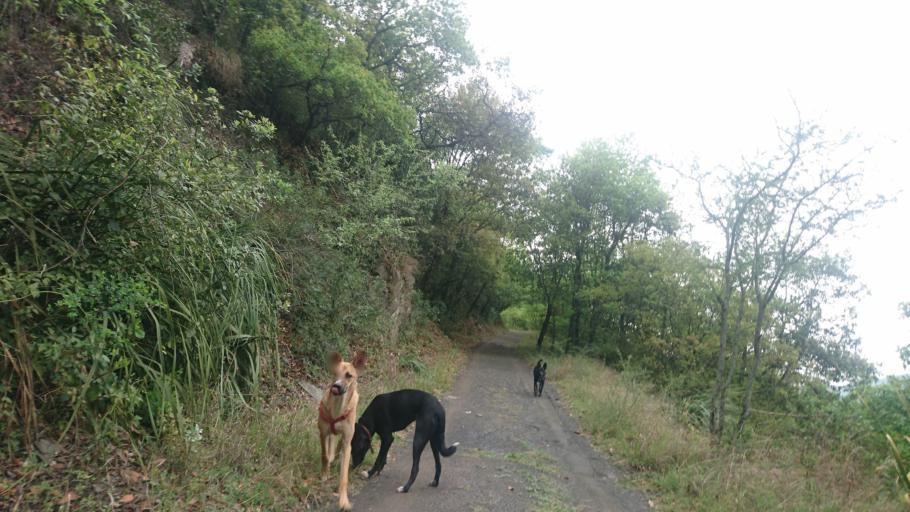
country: MX
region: Nuevo Leon
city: Garza Garcia
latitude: 25.6026
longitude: -100.3404
